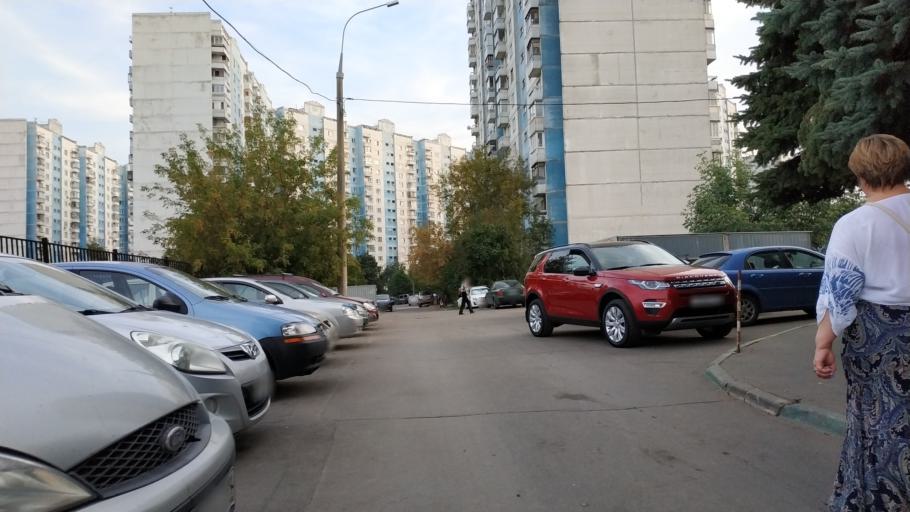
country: RU
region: Moscow
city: Solntsevo
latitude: 55.6444
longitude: 37.3679
